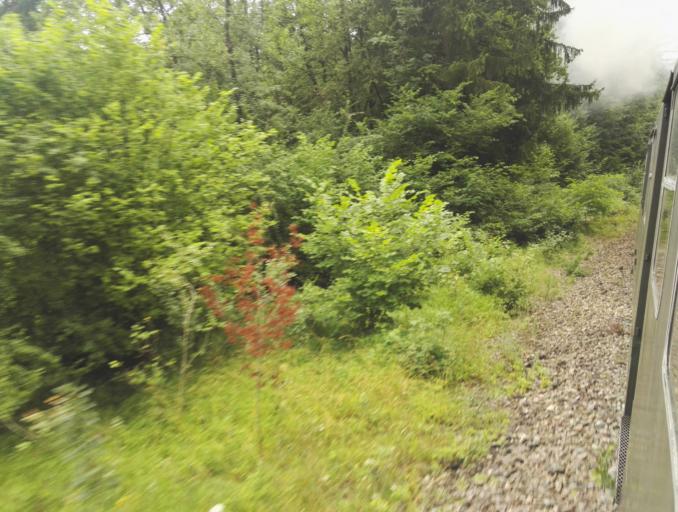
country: CH
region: Schaffhausen
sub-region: Bezirk Schleitheim
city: Schleitheim
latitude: 47.7899
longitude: 8.5138
